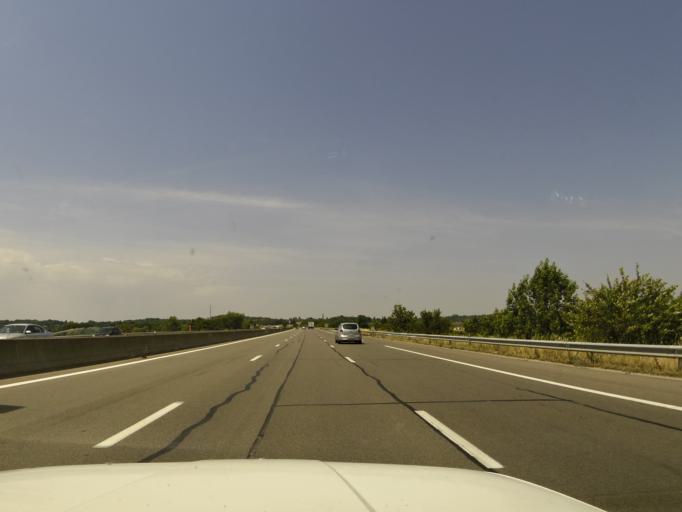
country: FR
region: Rhone-Alpes
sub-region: Departement de l'Ain
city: Beligneux
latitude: 45.8635
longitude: 5.1519
